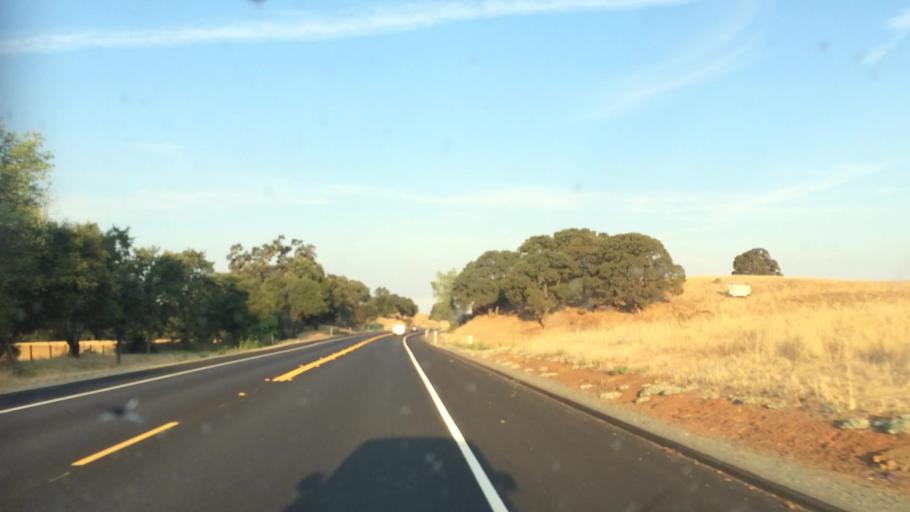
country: US
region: California
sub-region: Amador County
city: Plymouth
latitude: 38.4511
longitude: -120.8822
